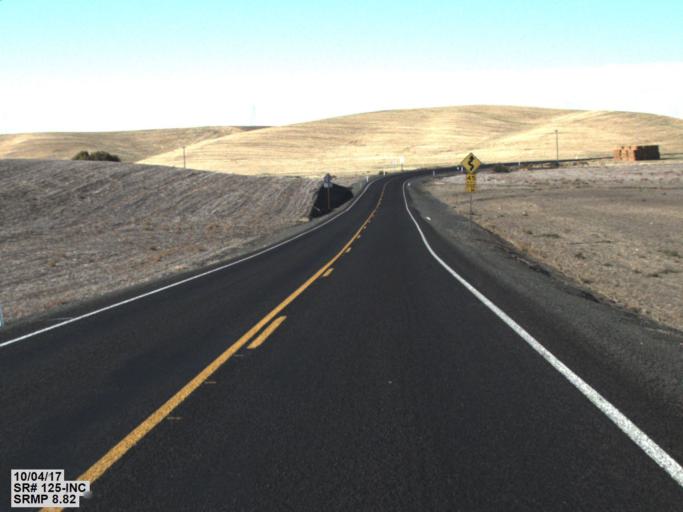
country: US
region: Washington
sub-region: Walla Walla County
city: Walla Walla
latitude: 46.1014
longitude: -118.3720
